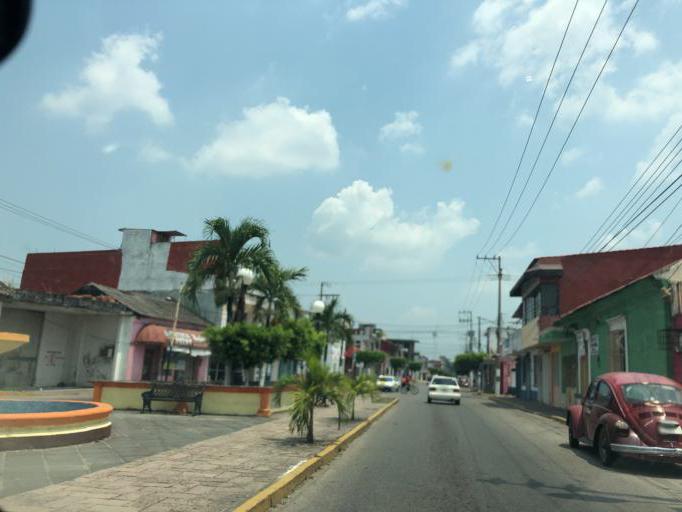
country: MX
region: Tabasco
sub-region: Cardenas
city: Cardenas
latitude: 17.9871
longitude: -93.3771
